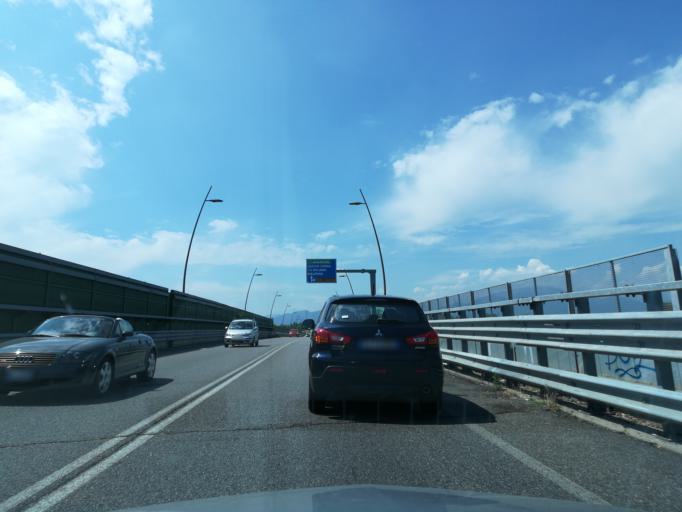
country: IT
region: Lombardy
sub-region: Provincia di Bergamo
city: Stezzano
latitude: 45.6414
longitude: 9.6369
